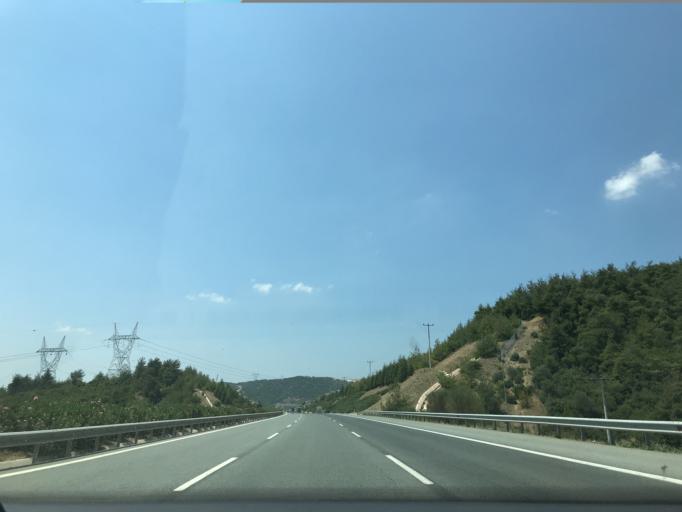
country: TR
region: Bursa
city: Gursu
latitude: 40.2507
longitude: 29.2369
